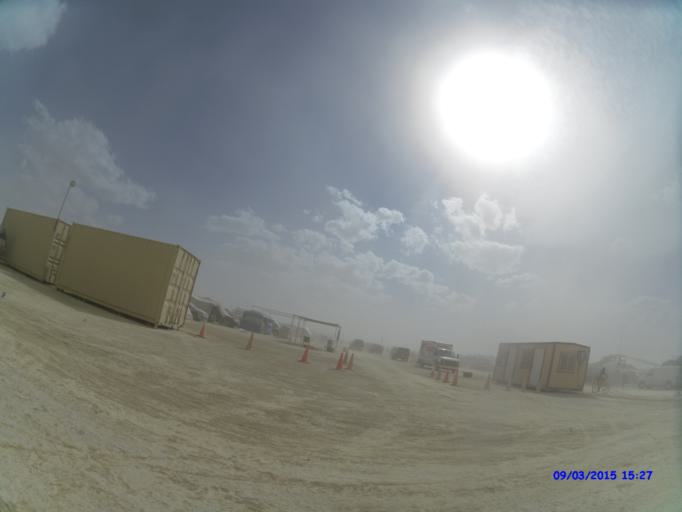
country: US
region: Nevada
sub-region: Pershing County
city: Lovelock
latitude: 40.7787
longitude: -119.2120
